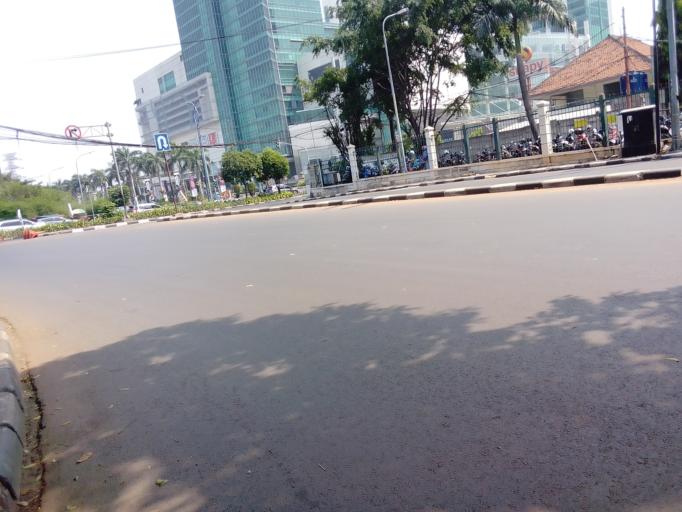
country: ID
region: Jakarta Raya
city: Jakarta
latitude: -6.2286
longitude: 106.7977
